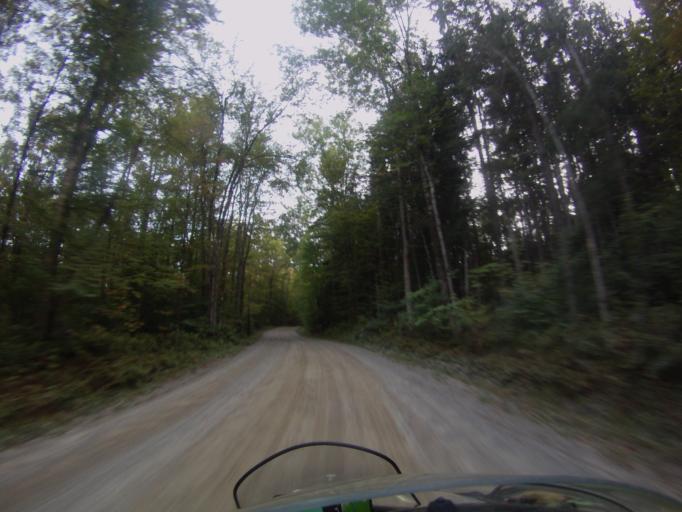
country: US
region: Vermont
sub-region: Addison County
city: Bristol
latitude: 44.0179
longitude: -73.0259
